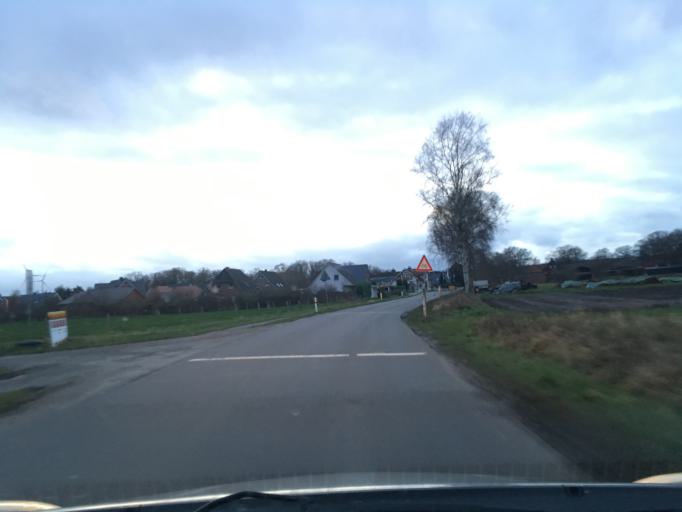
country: DE
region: Lower Saxony
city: Wulfsen
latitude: 53.3460
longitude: 10.1534
